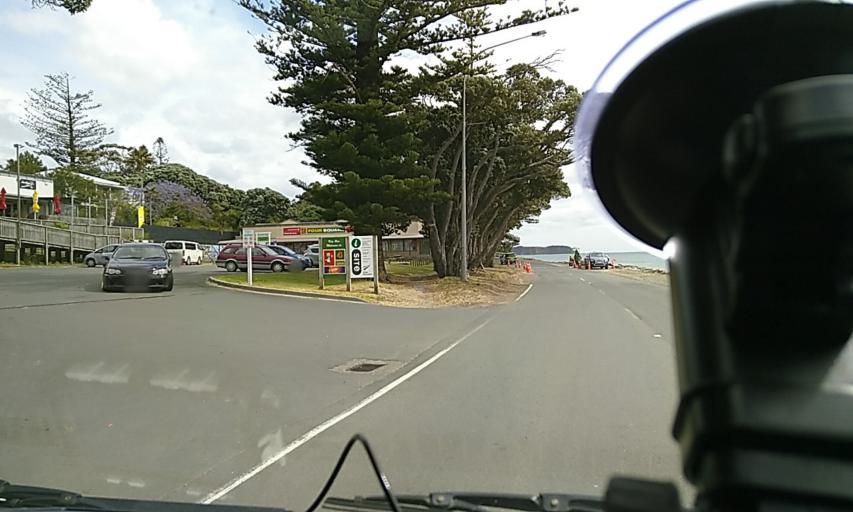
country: NZ
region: Northland
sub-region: Far North District
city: Ahipara
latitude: -35.5049
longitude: 173.3910
